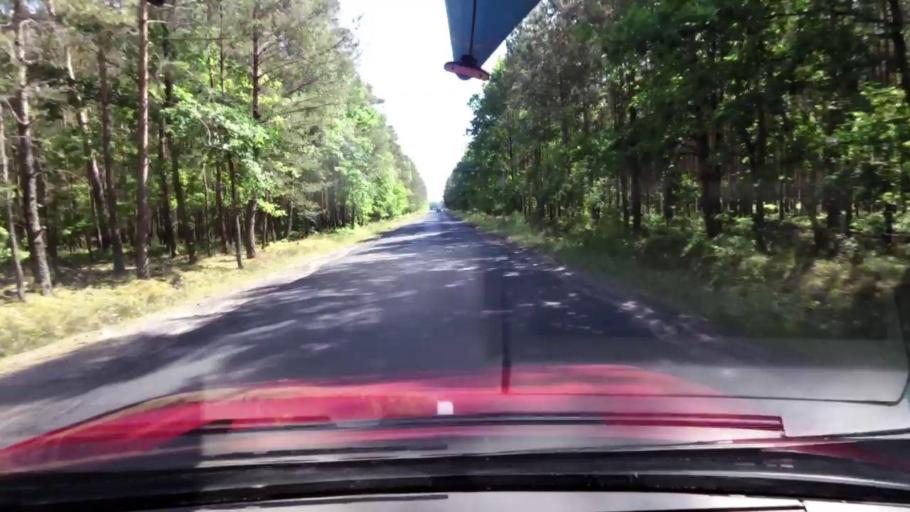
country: PL
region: Pomeranian Voivodeship
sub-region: Powiat slupski
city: Kepice
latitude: 54.3027
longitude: 16.9616
